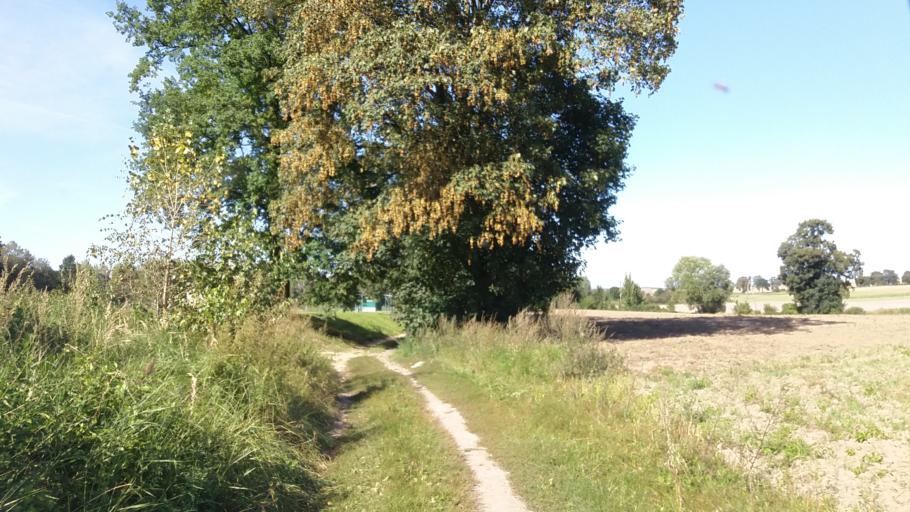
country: PL
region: West Pomeranian Voivodeship
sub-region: Powiat choszczenski
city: Krzecin
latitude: 53.1346
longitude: 15.5037
